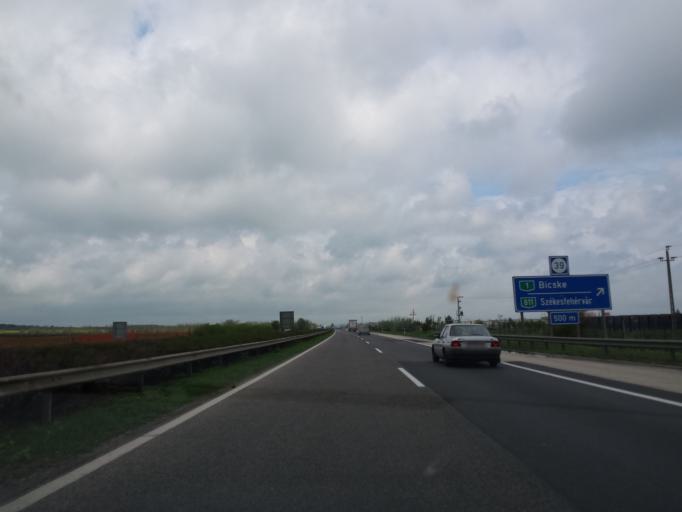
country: HU
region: Fejer
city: Bicske
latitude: 47.4959
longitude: 18.5871
